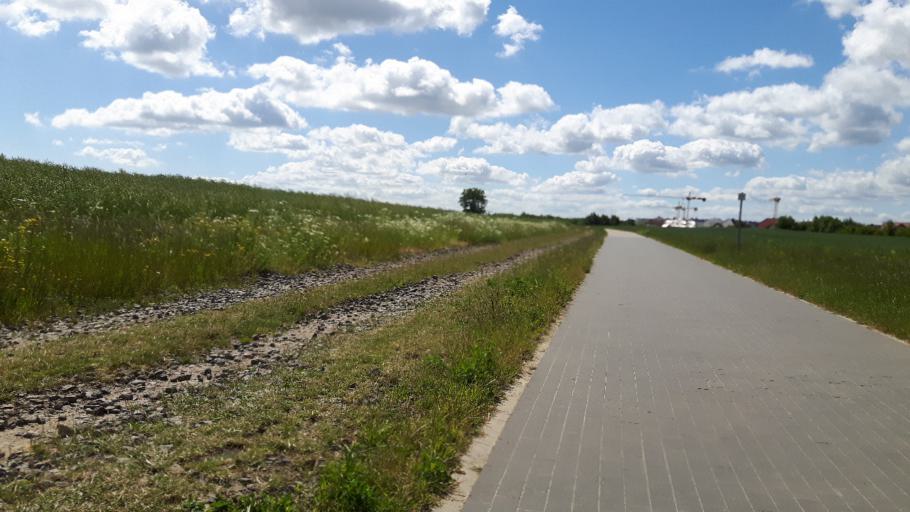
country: PL
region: Pomeranian Voivodeship
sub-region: Powiat pucki
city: Kosakowo
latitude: 54.5762
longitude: 18.4963
